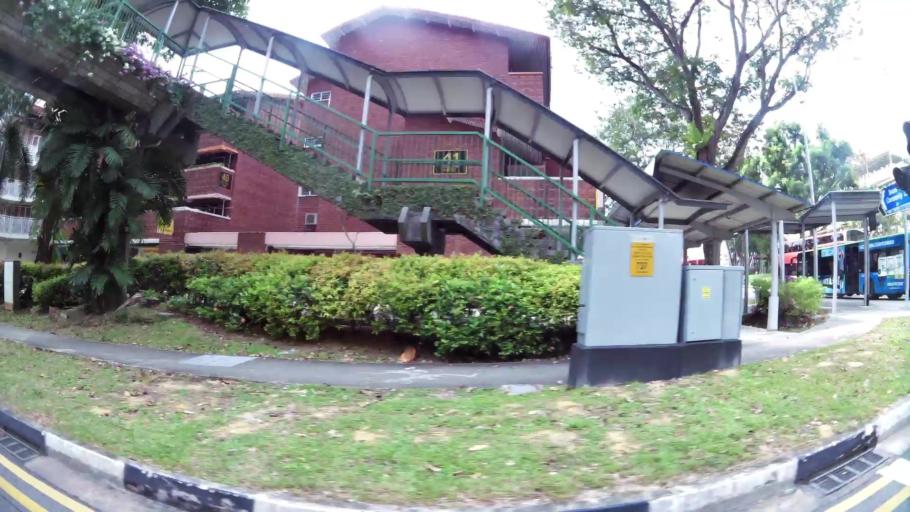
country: SG
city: Singapore
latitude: 1.3074
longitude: 103.7939
